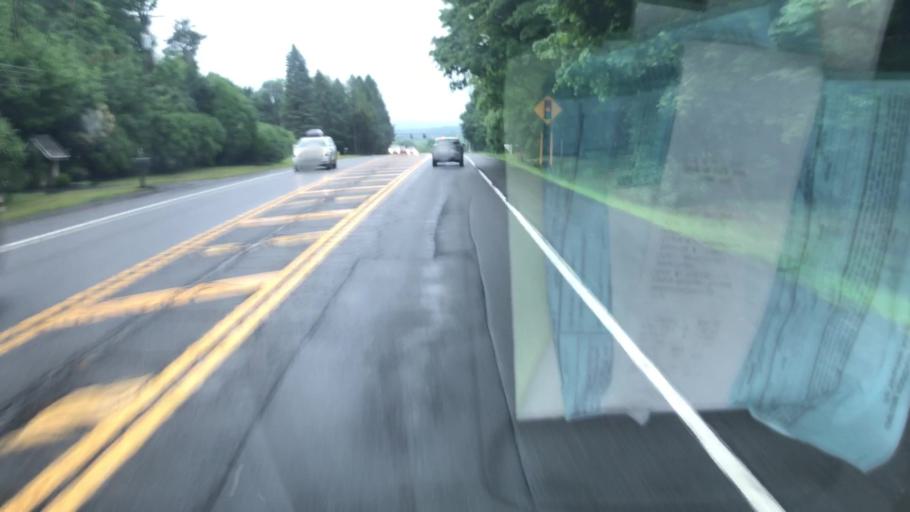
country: US
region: New York
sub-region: Onondaga County
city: Fayetteville
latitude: 43.0167
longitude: -76.0181
